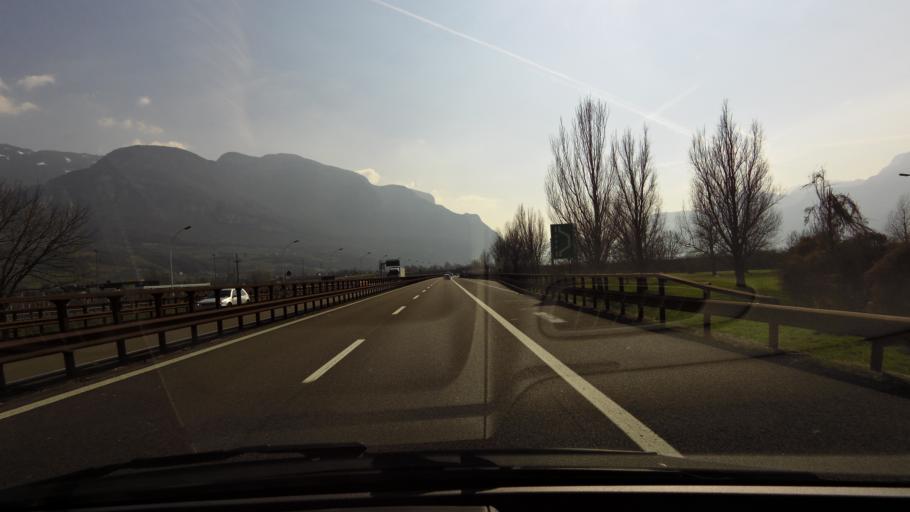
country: IT
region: Trentino-Alto Adige
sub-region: Bolzano
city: Egna
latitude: 46.3346
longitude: 11.2764
